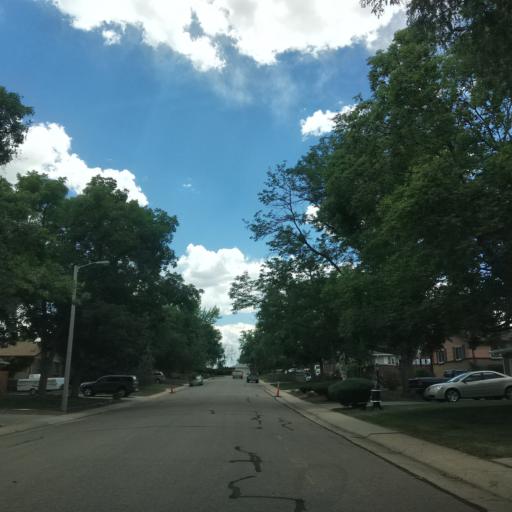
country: US
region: Colorado
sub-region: Jefferson County
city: Lakewood
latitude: 39.6875
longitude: -105.0881
